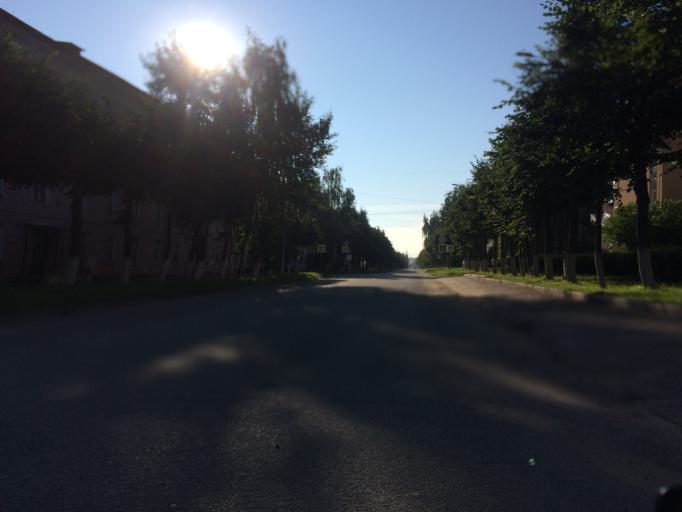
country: RU
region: Mariy-El
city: Yoshkar-Ola
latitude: 56.6409
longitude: 47.8827
